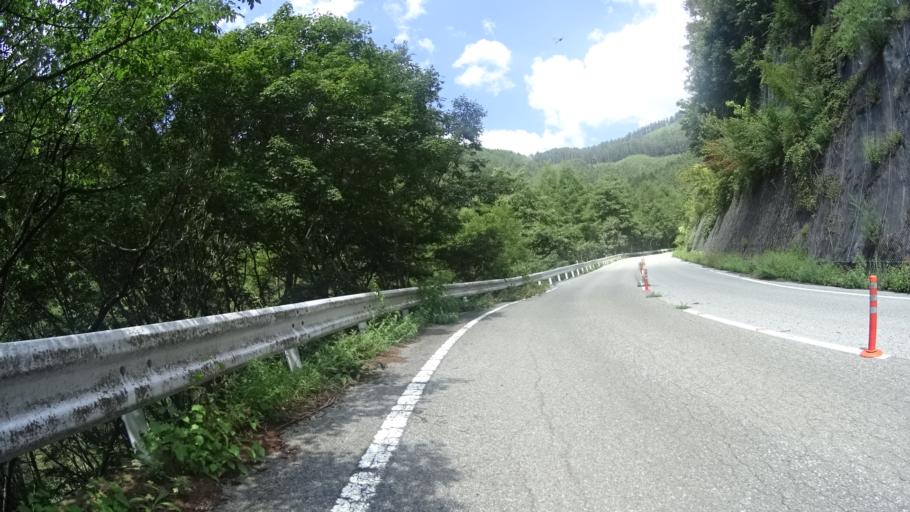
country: JP
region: Yamanashi
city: Enzan
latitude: 35.8024
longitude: 138.6714
